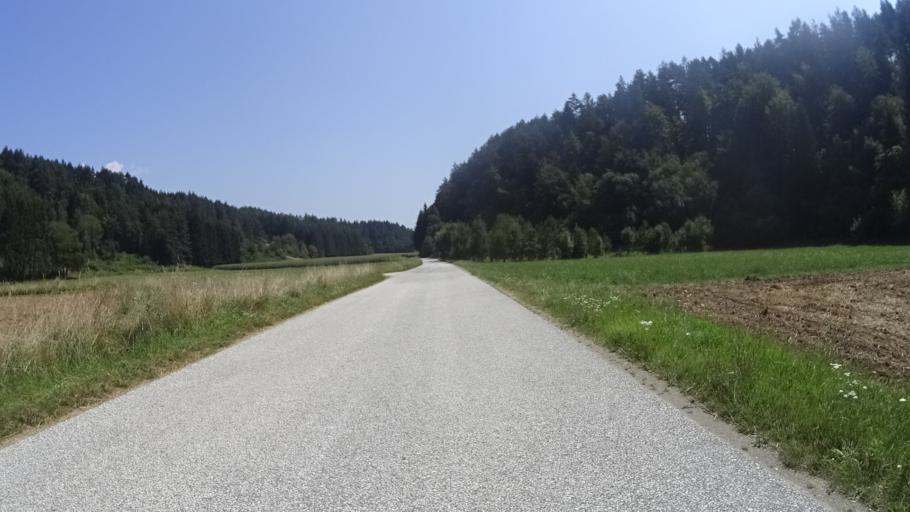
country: AT
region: Carinthia
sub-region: Politischer Bezirk Volkermarkt
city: Globasnitz
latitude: 46.5598
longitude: 14.6814
